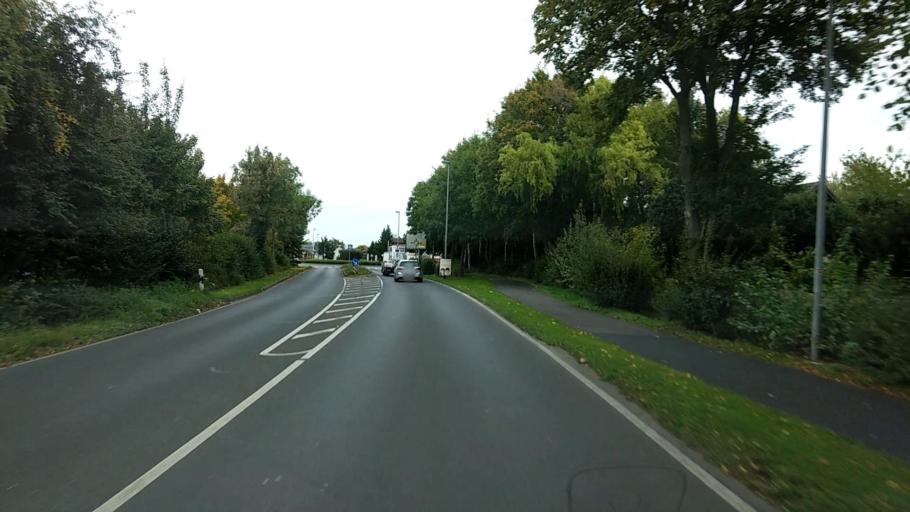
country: DE
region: North Rhine-Westphalia
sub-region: Regierungsbezirk Koln
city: Bergheim
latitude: 50.9457
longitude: 6.6278
